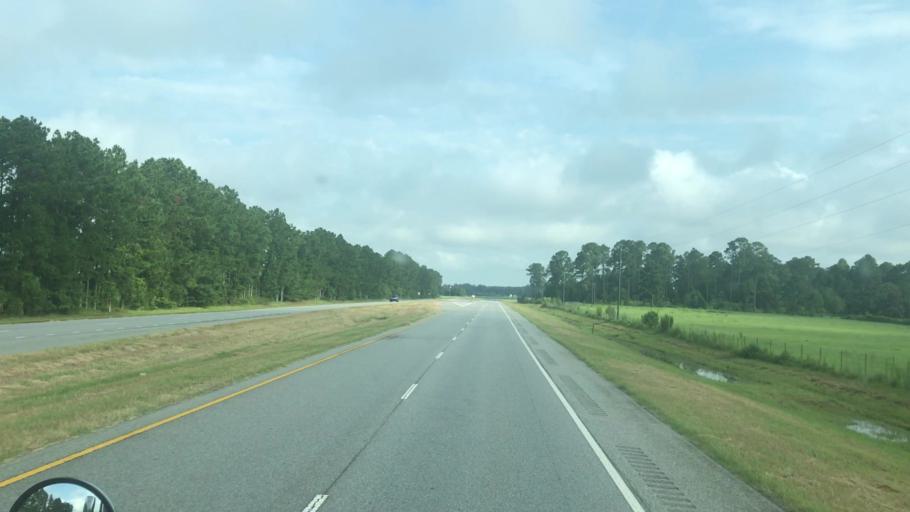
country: US
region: Georgia
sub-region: Miller County
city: Colquitt
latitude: 31.2102
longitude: -84.7742
